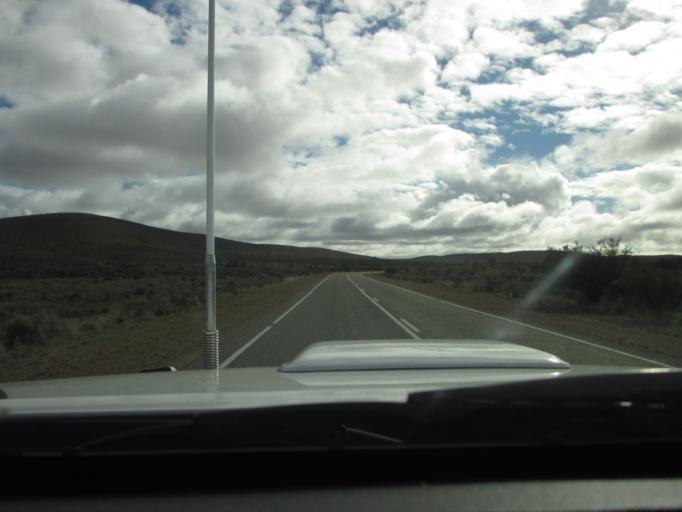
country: AU
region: South Australia
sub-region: Flinders Ranges
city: Quorn
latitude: -32.2148
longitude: 138.5191
